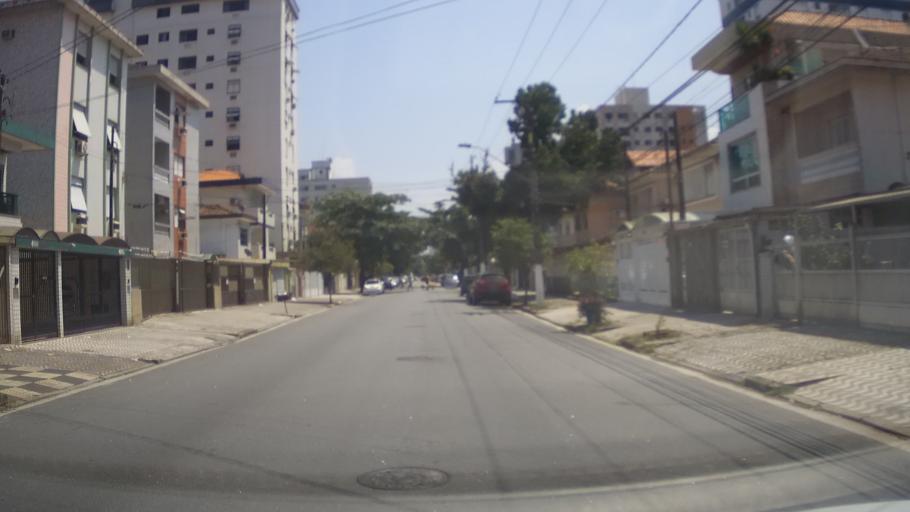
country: BR
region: Sao Paulo
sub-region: Santos
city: Santos
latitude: -23.9736
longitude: -46.3041
